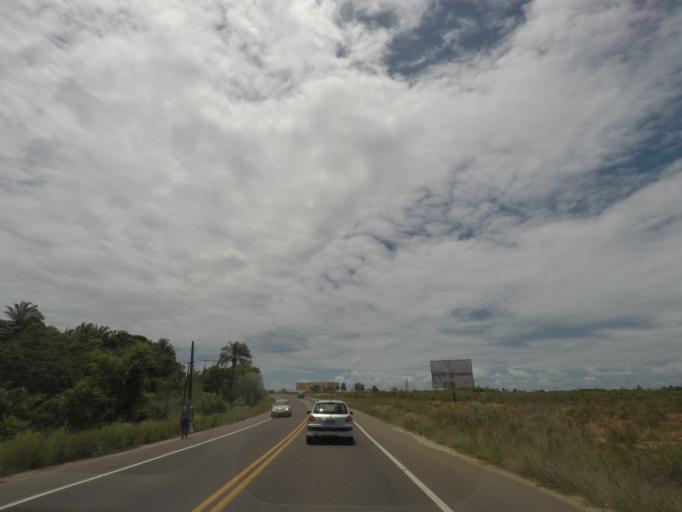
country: BR
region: Bahia
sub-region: Itaparica
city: Itaparica
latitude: -12.9408
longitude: -38.6304
